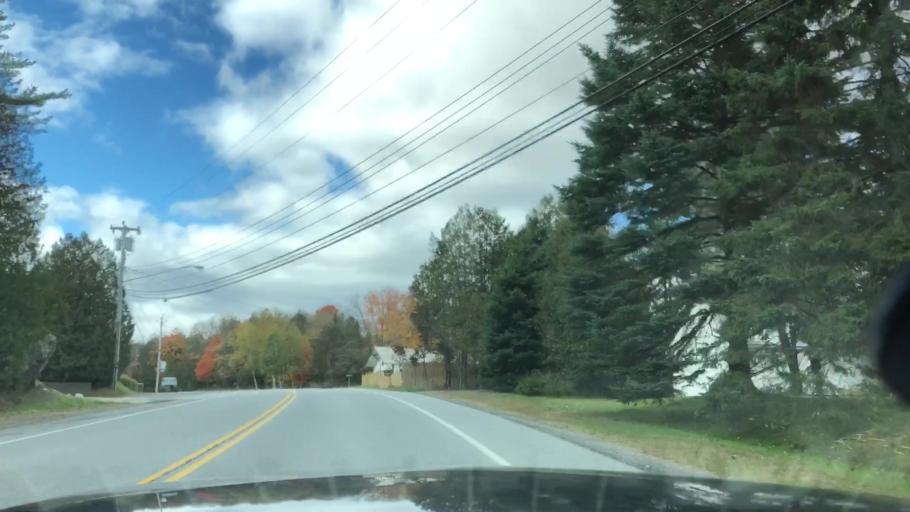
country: US
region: New York
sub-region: Essex County
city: Lake Placid
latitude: 43.9711
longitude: -74.1495
